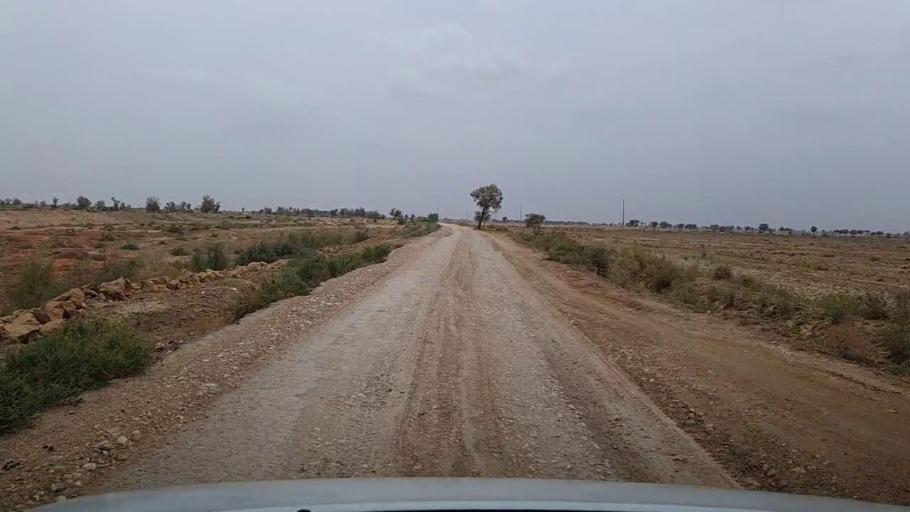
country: PK
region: Sindh
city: Sehwan
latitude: 26.3564
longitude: 67.7970
